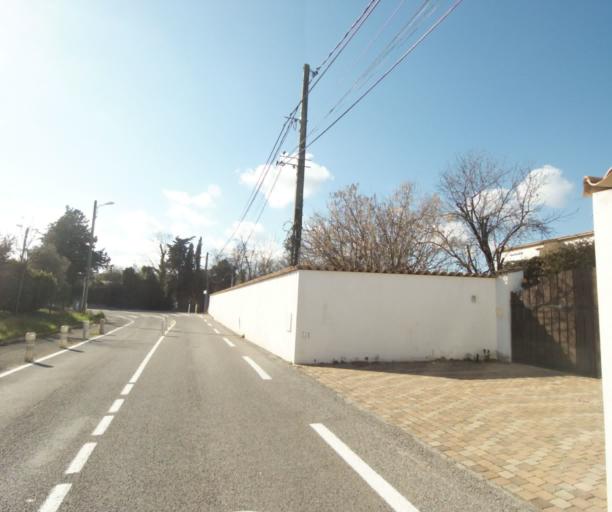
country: FR
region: Provence-Alpes-Cote d'Azur
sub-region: Departement des Alpes-Maritimes
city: Biot
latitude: 43.6170
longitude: 7.1220
